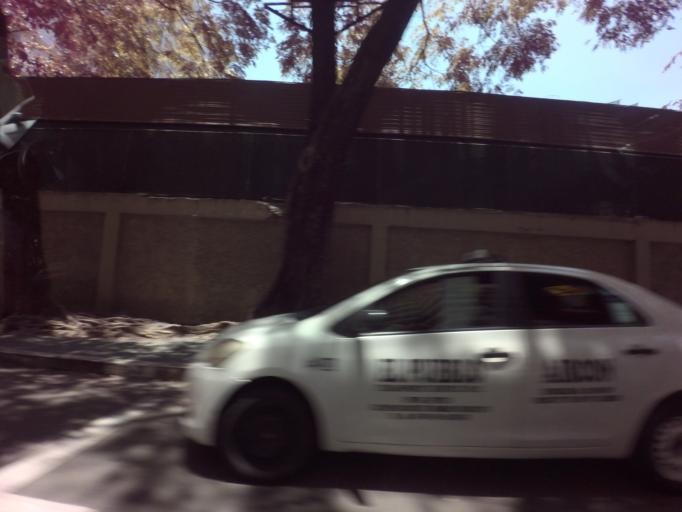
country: PH
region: Metro Manila
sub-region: Makati City
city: Makati City
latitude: 14.5602
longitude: 121.0215
